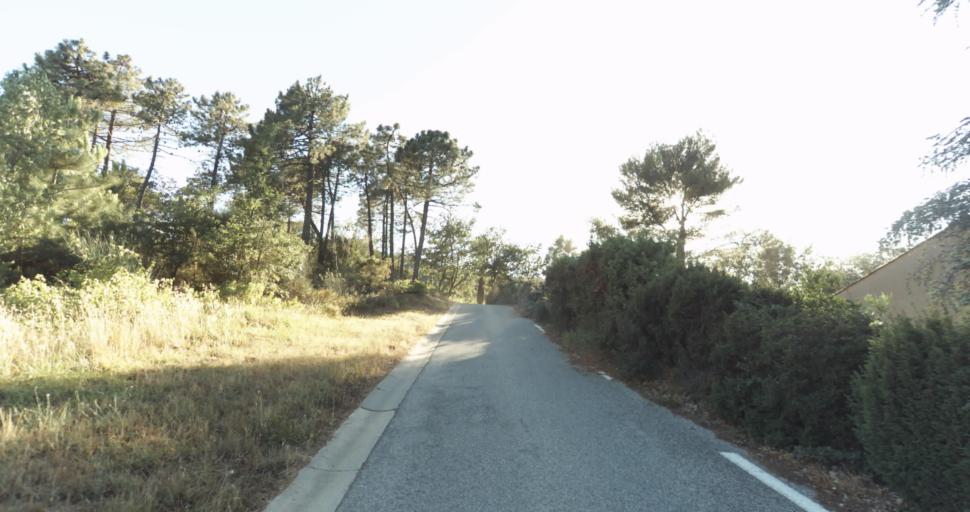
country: FR
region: Provence-Alpes-Cote d'Azur
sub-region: Departement du Var
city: Gassin
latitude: 43.2319
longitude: 6.5932
